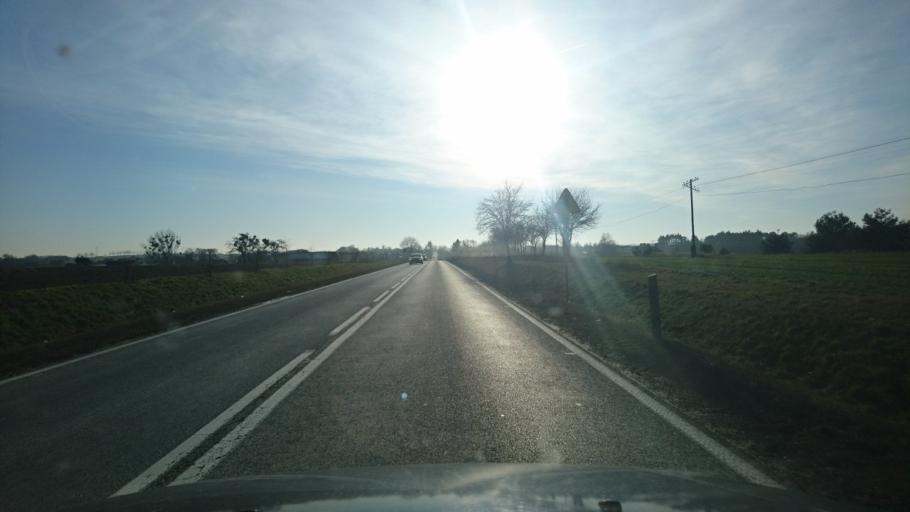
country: PL
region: Opole Voivodeship
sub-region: Powiat oleski
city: Dalachow
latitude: 51.0590
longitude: 18.5995
